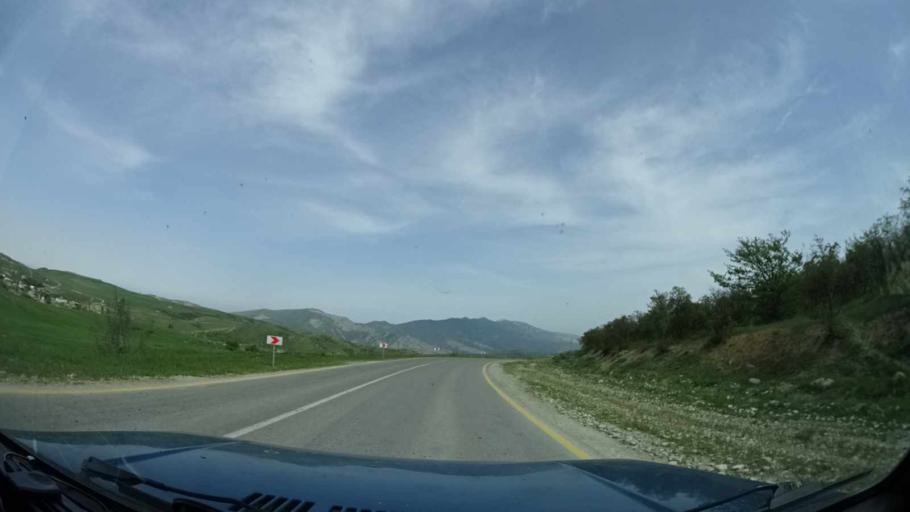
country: AZ
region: Xizi
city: Khyzy
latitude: 40.9075
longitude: 49.0971
